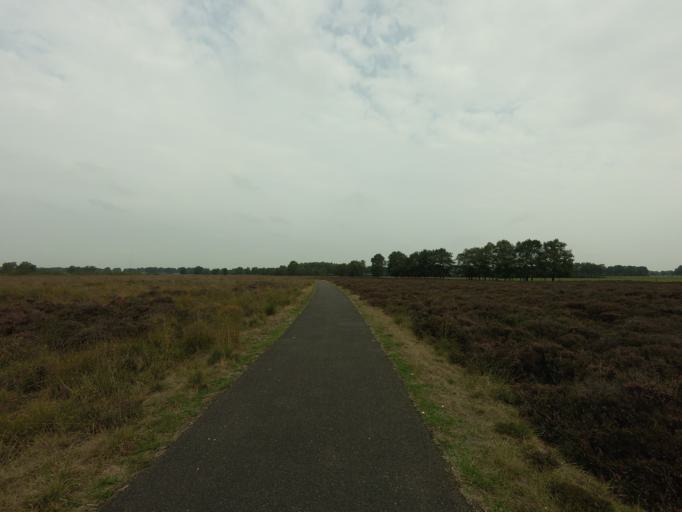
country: NL
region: Drenthe
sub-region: Gemeente Westerveld
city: Dwingeloo
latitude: 52.8812
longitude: 6.4651
